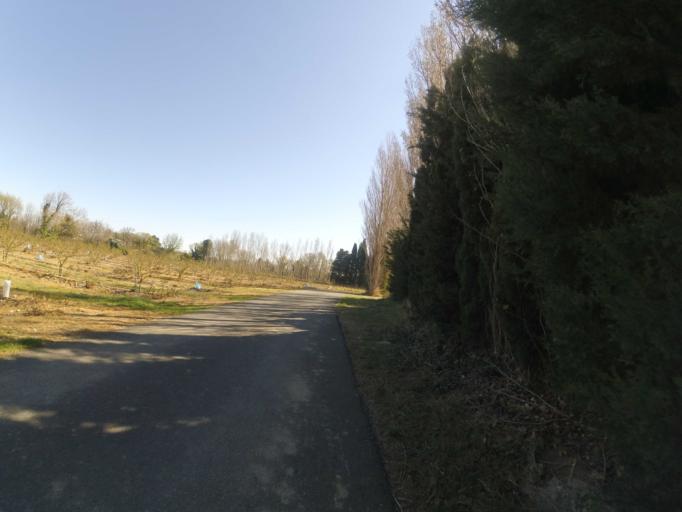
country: FR
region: Languedoc-Roussillon
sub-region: Departement des Pyrenees-Orientales
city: Corneilla-la-Riviere
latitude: 42.6843
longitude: 2.7150
